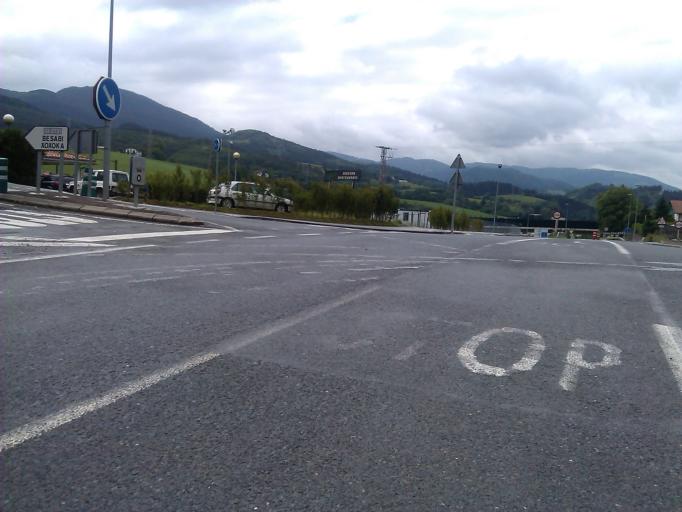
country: ES
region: Basque Country
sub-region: Provincia de Guipuzcoa
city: Urnieta
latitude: 43.2357
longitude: -1.9993
